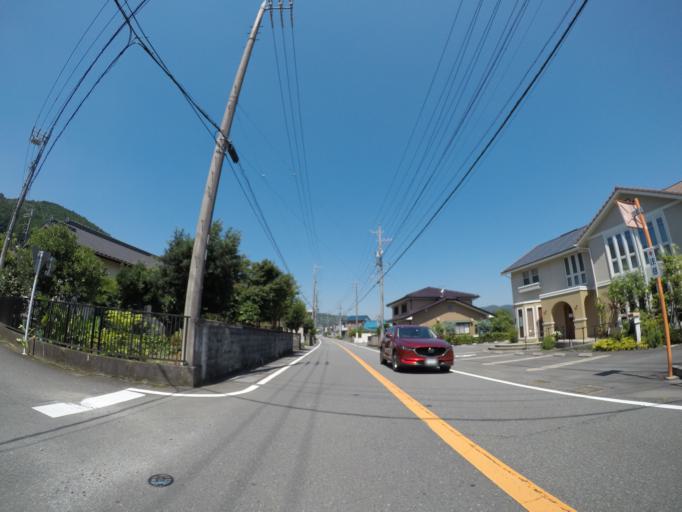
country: JP
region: Shizuoka
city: Fujinomiya
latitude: 35.1846
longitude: 138.5971
